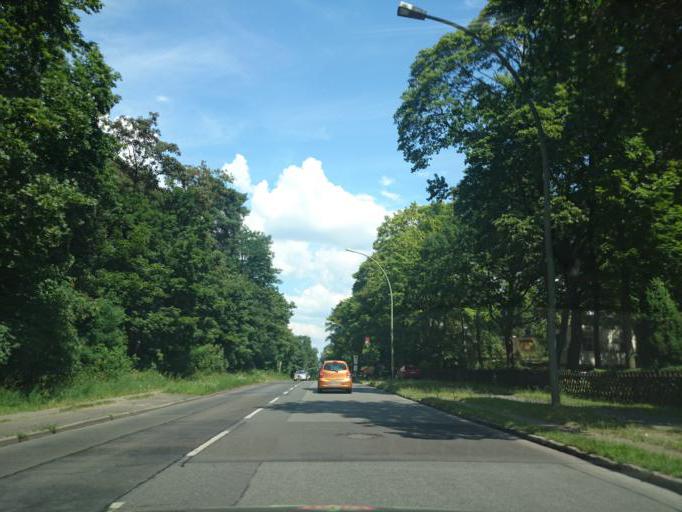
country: DE
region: Berlin
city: Gatow
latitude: 52.4731
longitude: 13.1730
